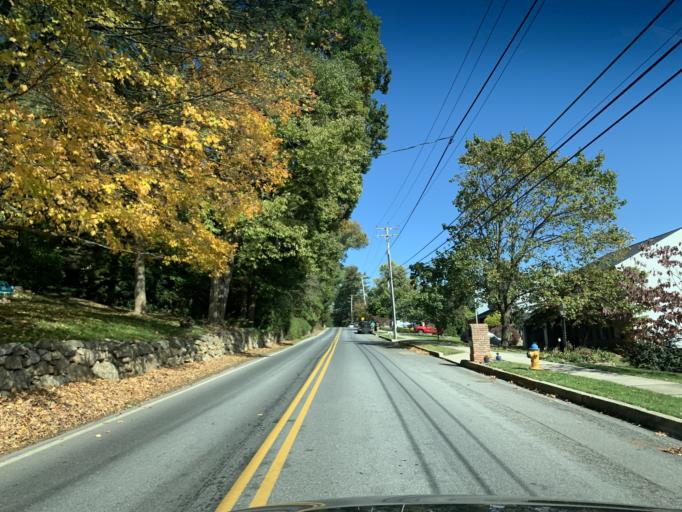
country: US
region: Pennsylvania
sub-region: Berks County
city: Reiffton
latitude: 40.3161
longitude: -75.8818
